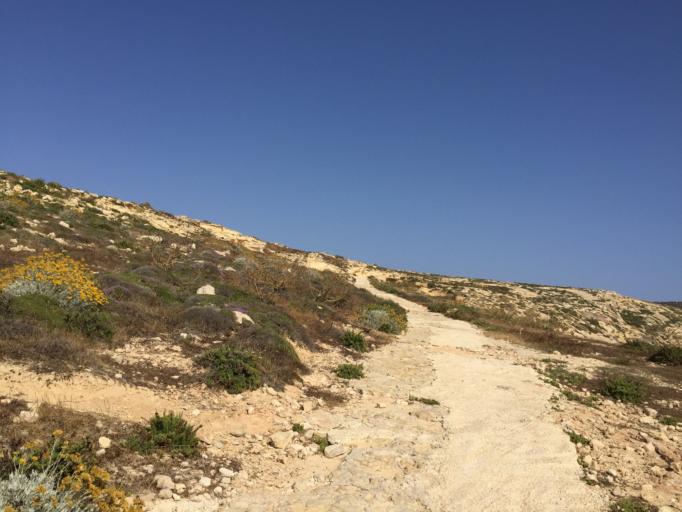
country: MT
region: Saint Lawrence
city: San Lawrenz
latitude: 36.0490
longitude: 14.1917
